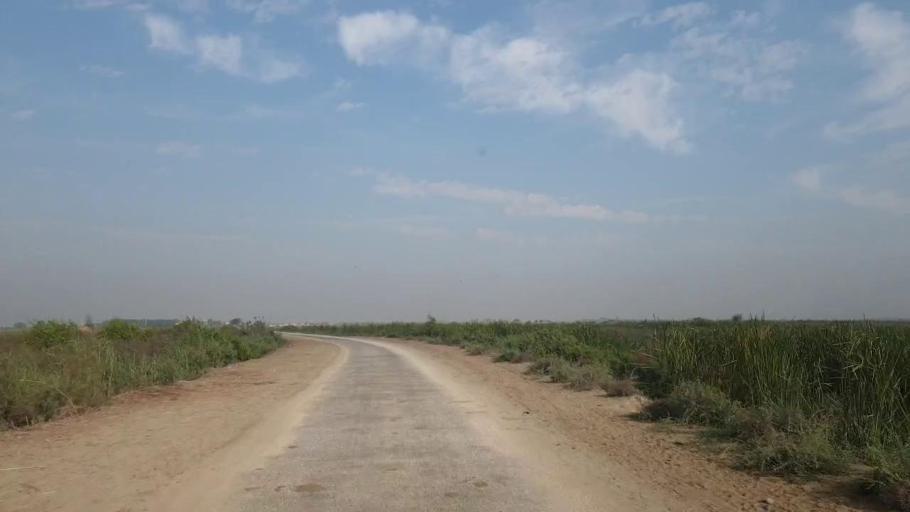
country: PK
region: Sindh
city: Tando Bago
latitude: 24.8505
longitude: 68.9713
